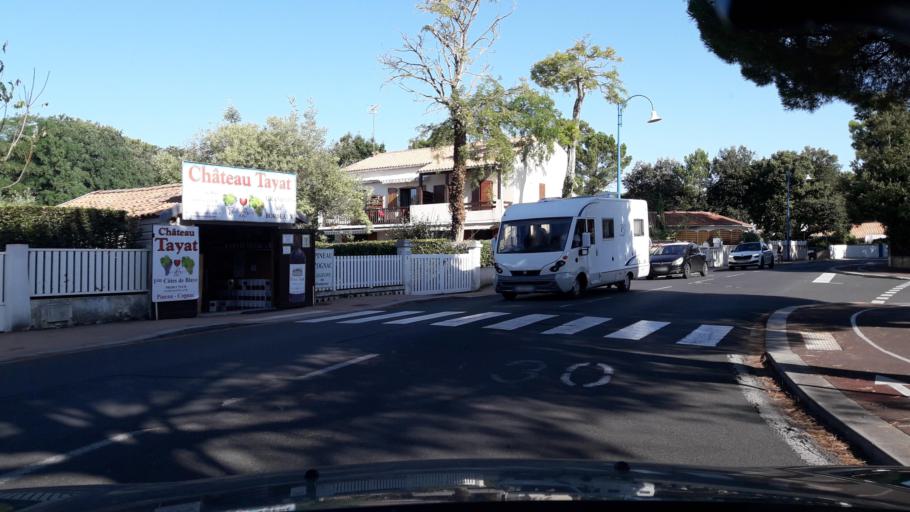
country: FR
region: Poitou-Charentes
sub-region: Departement de la Charente-Maritime
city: Les Mathes
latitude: 45.6917
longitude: -1.1793
